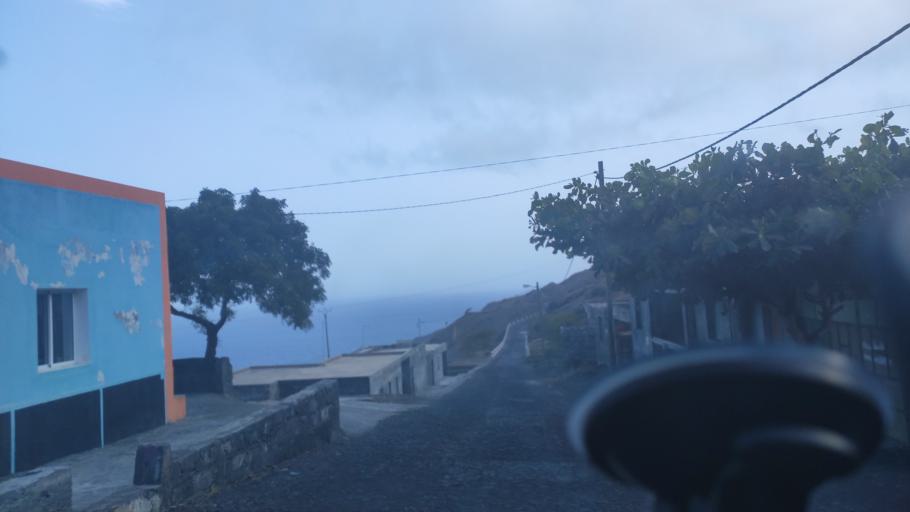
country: CV
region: Mosteiros
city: Porto dos Mosteiros
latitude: 15.0052
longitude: -24.3037
